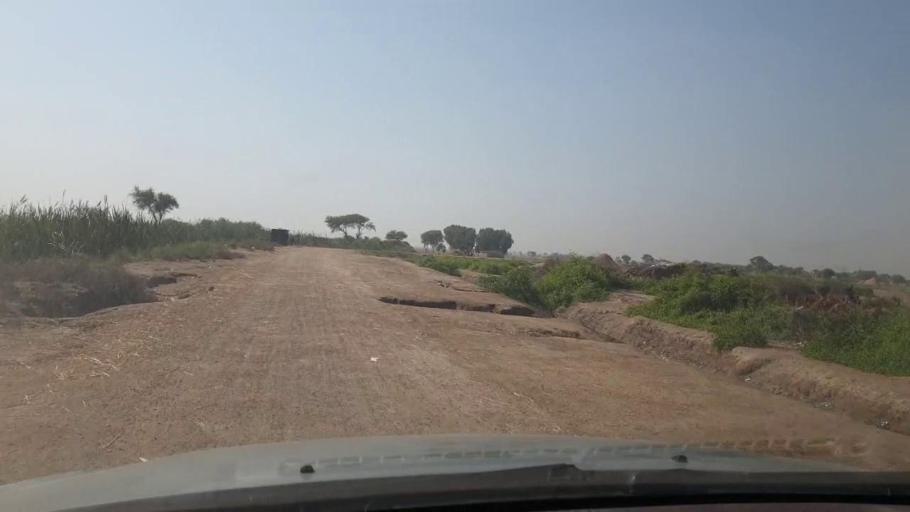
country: PK
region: Sindh
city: Bulri
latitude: 24.9068
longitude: 68.4345
